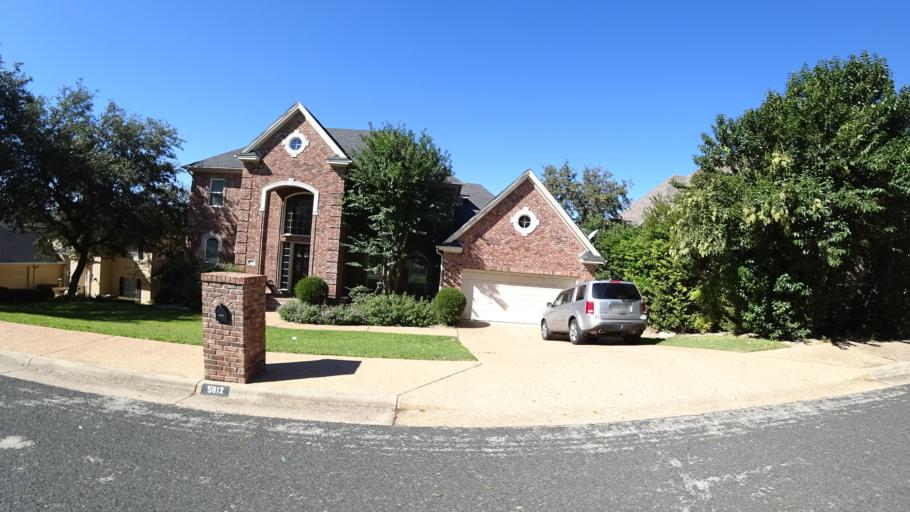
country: US
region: Texas
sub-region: Travis County
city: West Lake Hills
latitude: 30.3435
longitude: -97.7723
